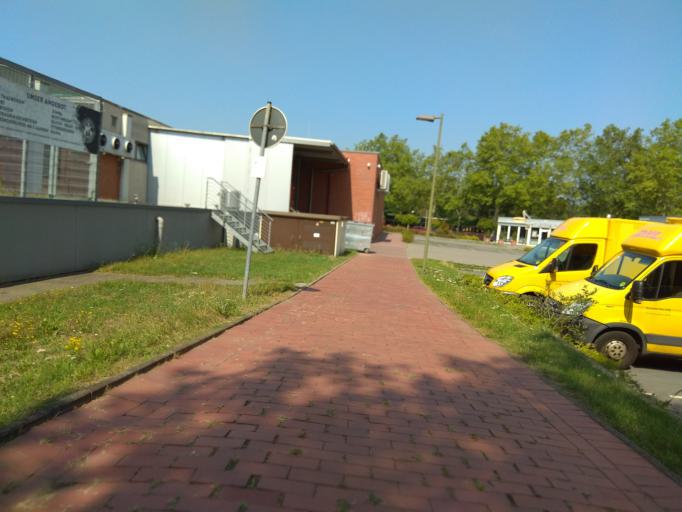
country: DE
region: North Rhine-Westphalia
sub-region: Regierungsbezirk Munster
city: Klein Reken
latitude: 51.7257
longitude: 7.0276
